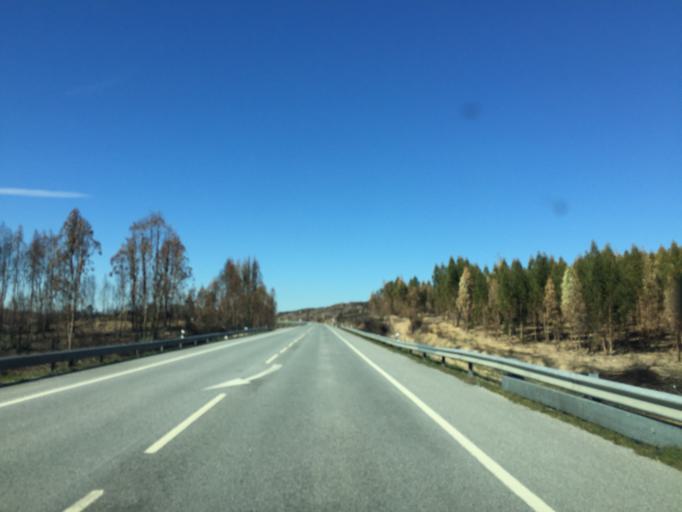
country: PT
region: Portalegre
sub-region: Nisa
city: Nisa
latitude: 39.5201
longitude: -7.7738
